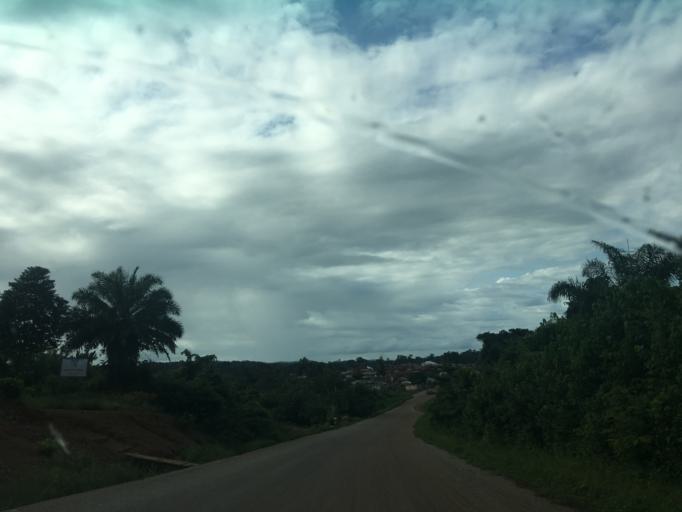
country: GH
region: Western
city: Wassa-Akropong
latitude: 5.9997
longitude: -2.4107
